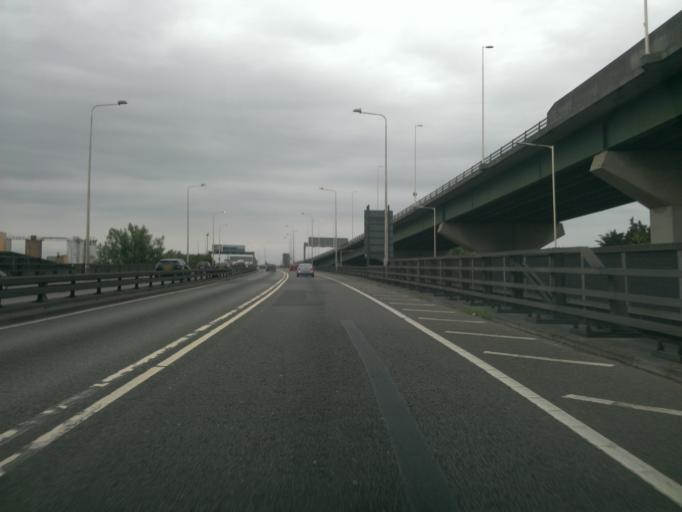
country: GB
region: England
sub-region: Kent
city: West Thurrock
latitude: 51.4746
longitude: 0.2658
